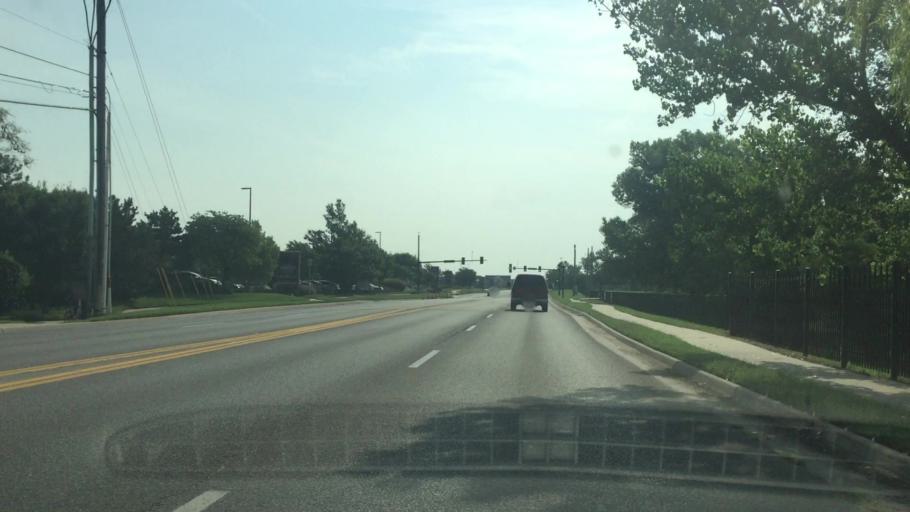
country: US
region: Kansas
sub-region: Sedgwick County
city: Bellaire
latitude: 37.7084
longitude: -97.2246
